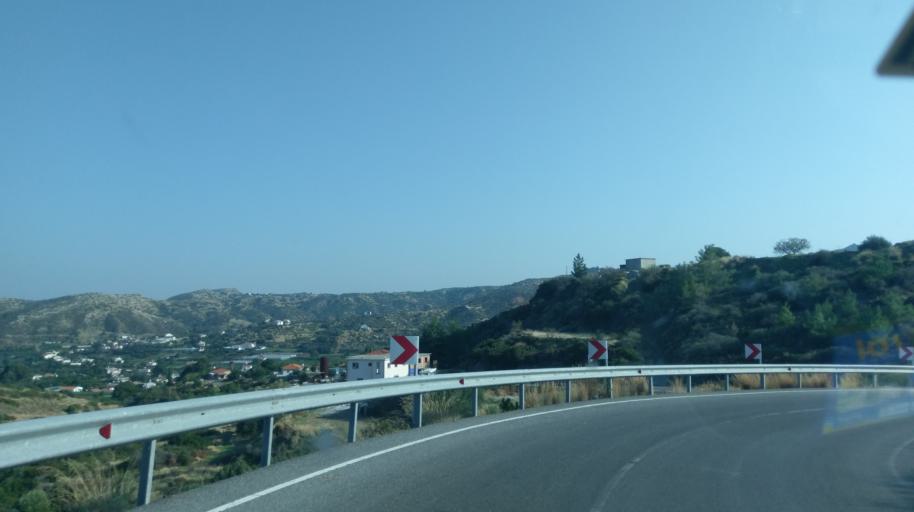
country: CY
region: Lefkosia
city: Kato Pyrgos
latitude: 35.1688
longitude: 32.7280
